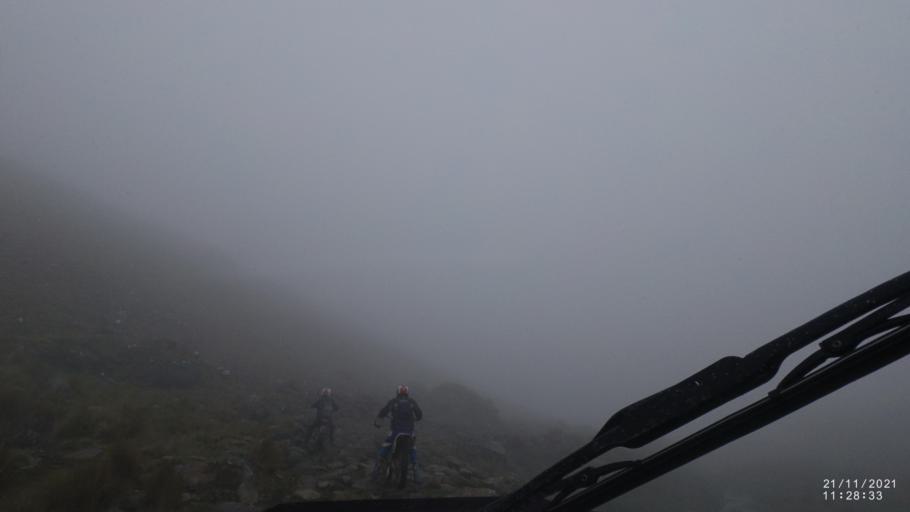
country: BO
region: Cochabamba
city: Cochabamba
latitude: -16.9612
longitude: -66.2683
